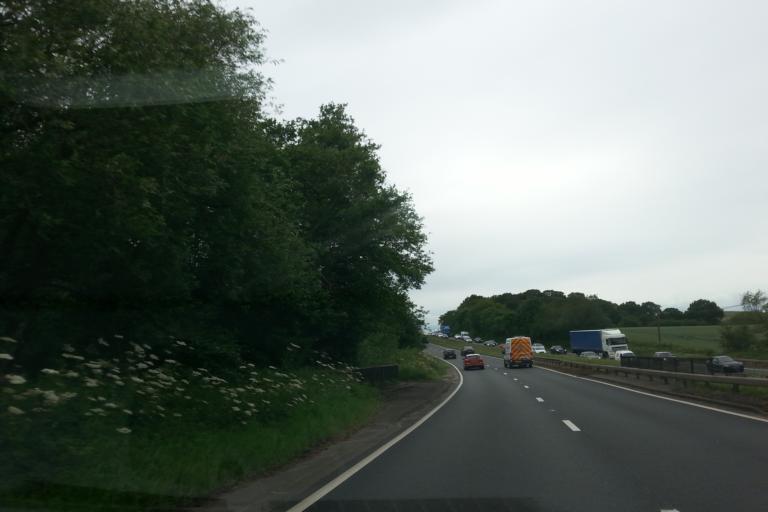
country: GB
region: England
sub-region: Solihull
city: Hampton in Arden
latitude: 52.4495
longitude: -1.6915
